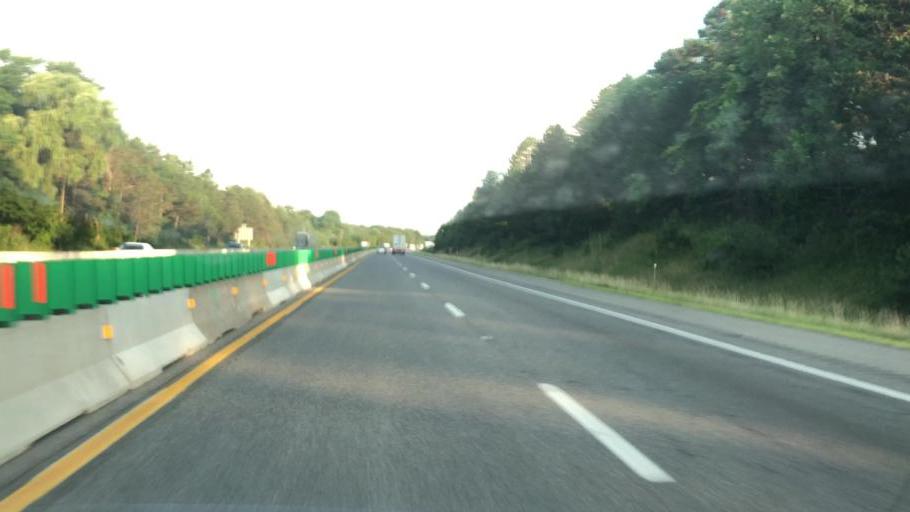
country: US
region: Ohio
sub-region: Cuyahoga County
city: Broadview Heights
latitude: 41.2957
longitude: -81.6857
